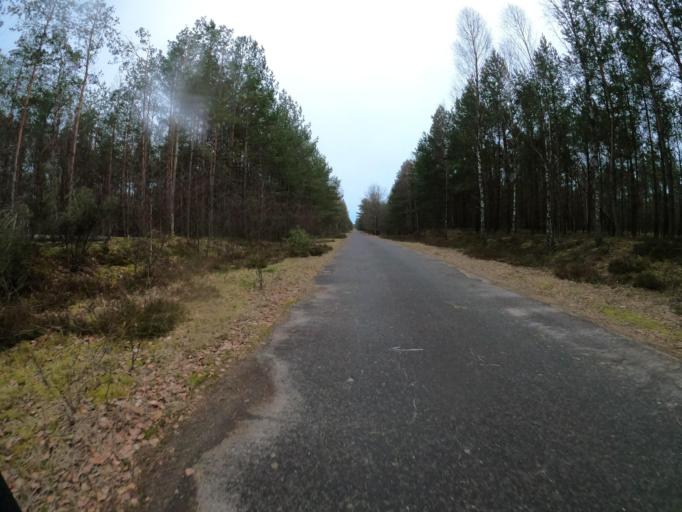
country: PL
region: West Pomeranian Voivodeship
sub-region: Powiat szczecinecki
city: Borne Sulinowo
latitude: 53.5596
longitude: 16.5765
